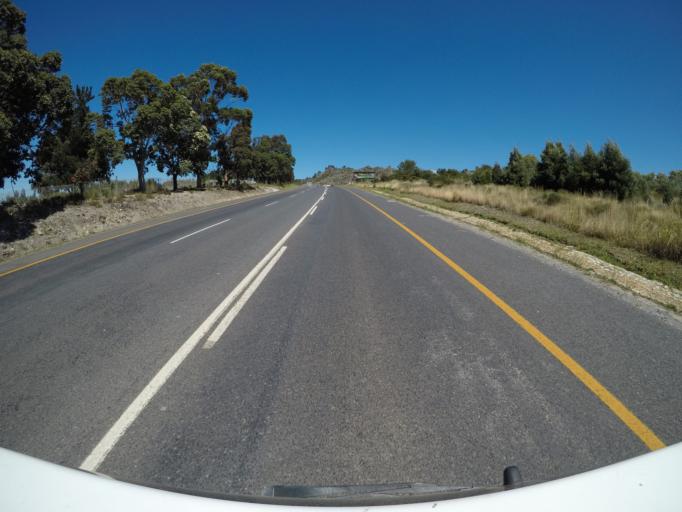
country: ZA
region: Western Cape
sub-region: Overberg District Municipality
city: Grabouw
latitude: -34.1624
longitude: 19.0117
